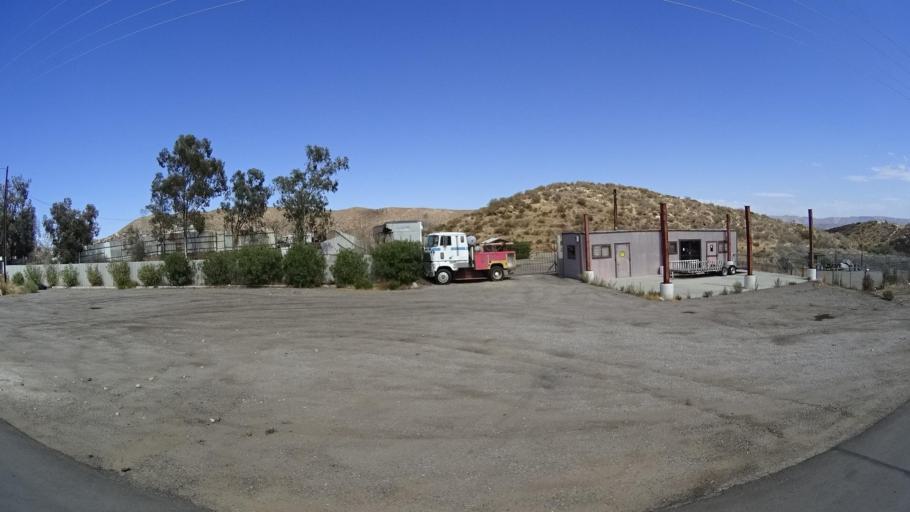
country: MX
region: Baja California
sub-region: Tecate
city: Cereso del Hongo
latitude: 32.6405
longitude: -116.2292
